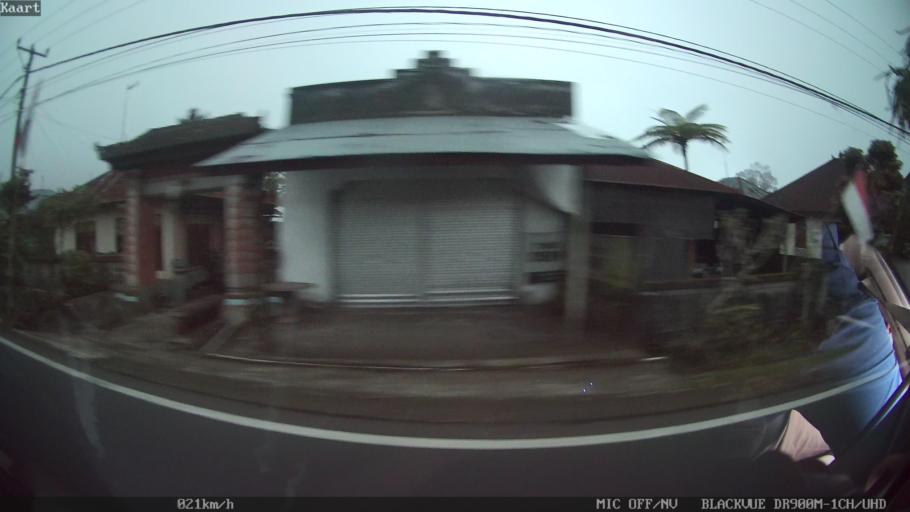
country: ID
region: Bali
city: Banjar Kedisan
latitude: -8.3034
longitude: 115.3078
